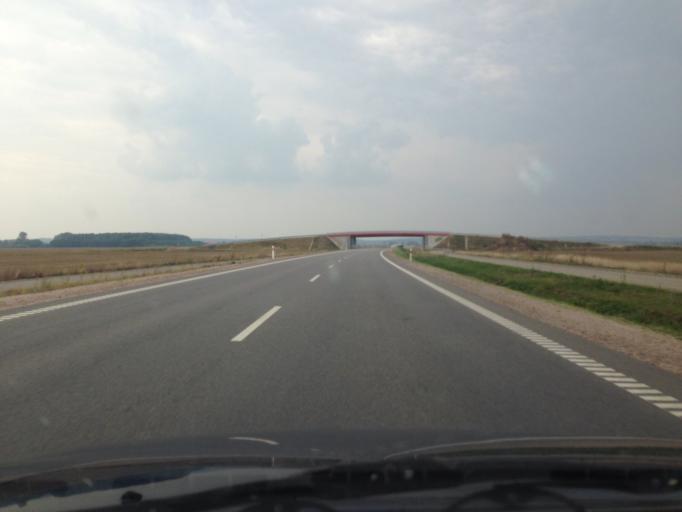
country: PL
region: Pomeranian Voivodeship
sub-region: Powiat kwidzynski
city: Kwidzyn
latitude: 53.7544
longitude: 18.9001
